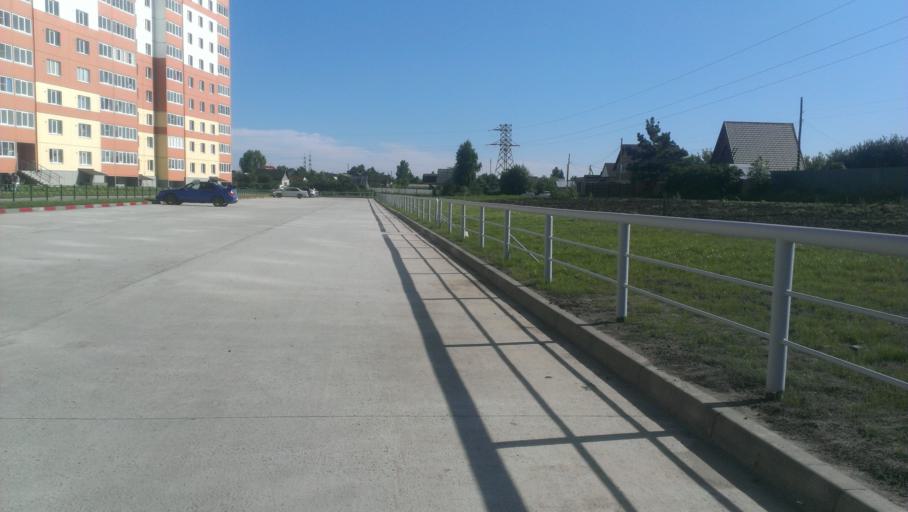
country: RU
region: Altai Krai
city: Novosilikatnyy
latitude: 53.3271
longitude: 83.6672
